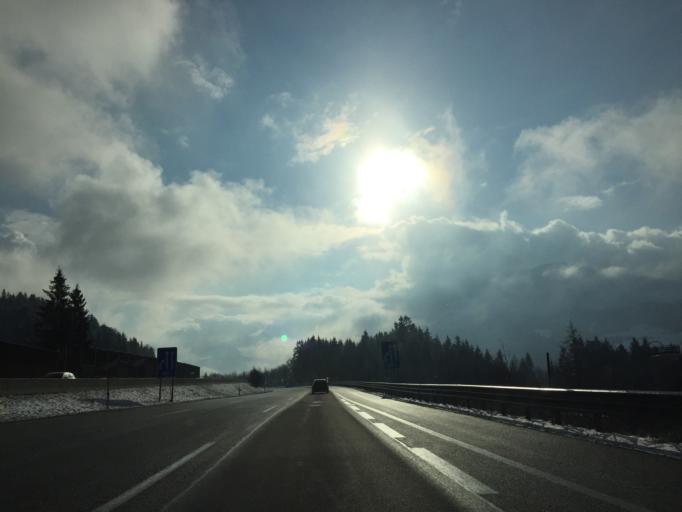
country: AT
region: Salzburg
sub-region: Politischer Bezirk Sankt Johann im Pongau
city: Werfenweng
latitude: 47.4372
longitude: 13.2413
